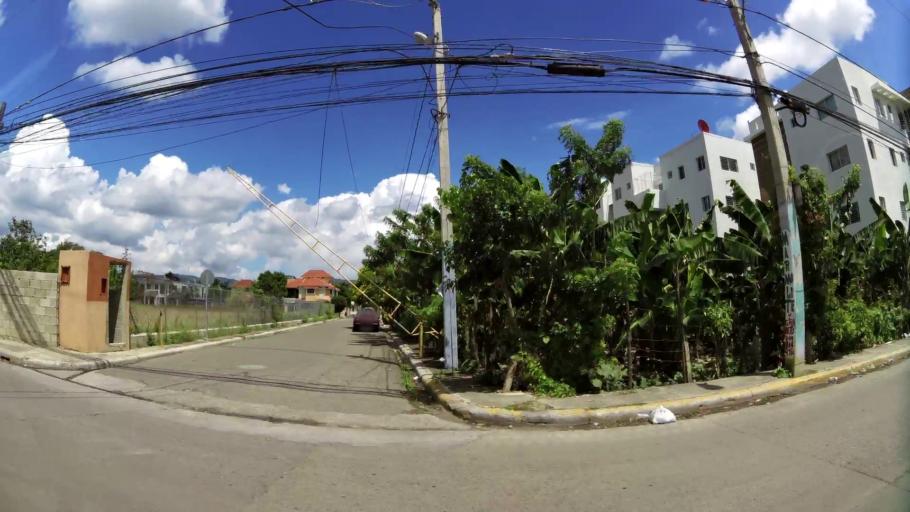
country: DO
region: Santiago
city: Santiago de los Caballeros
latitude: 19.4729
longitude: -70.6664
